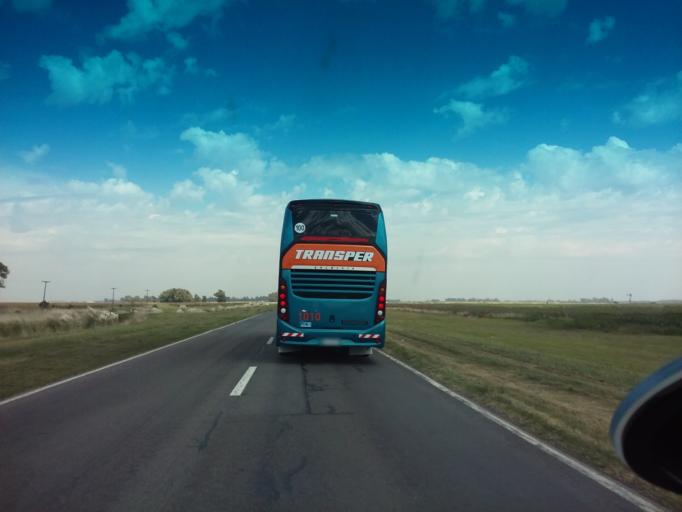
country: AR
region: Buenos Aires
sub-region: Partido de Carlos Casares
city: Carlos Casares
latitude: -35.6518
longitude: -61.3870
